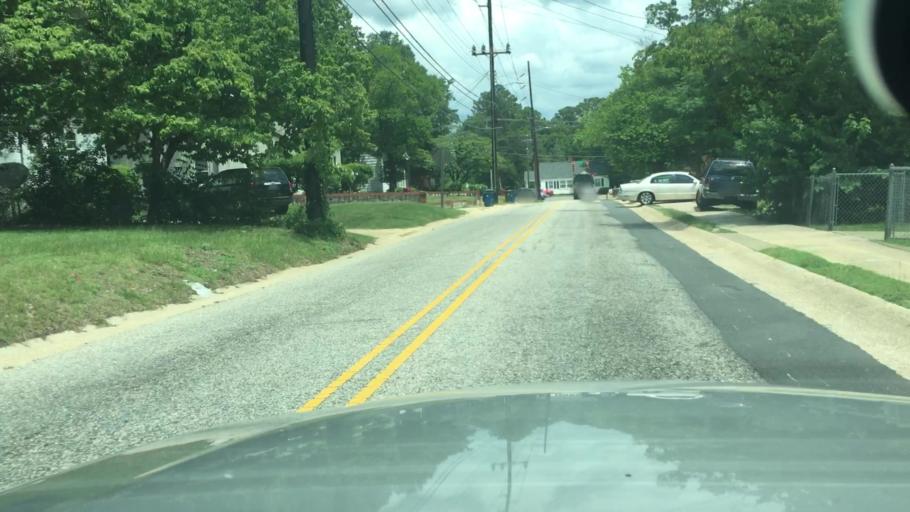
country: US
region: North Carolina
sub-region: Cumberland County
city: Fayetteville
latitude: 35.0801
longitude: -78.8835
